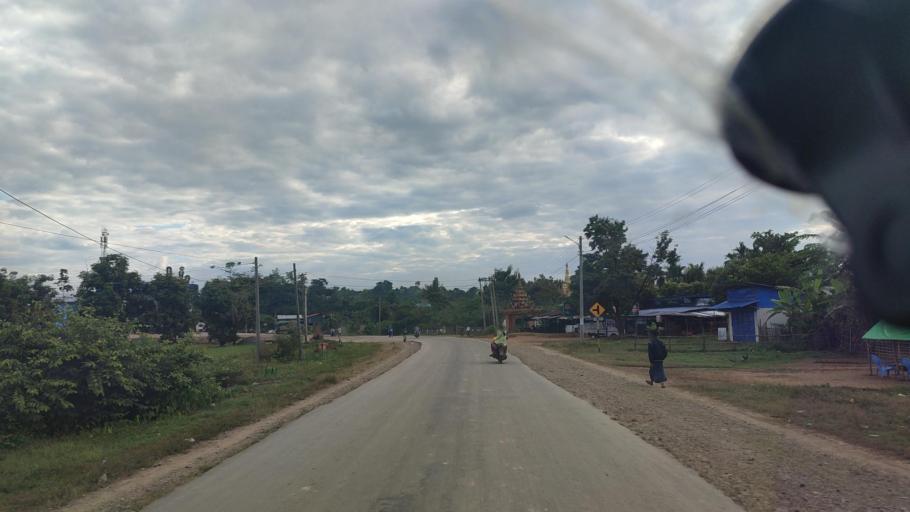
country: MM
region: Magway
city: Minbu
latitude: 19.7634
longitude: 94.0333
